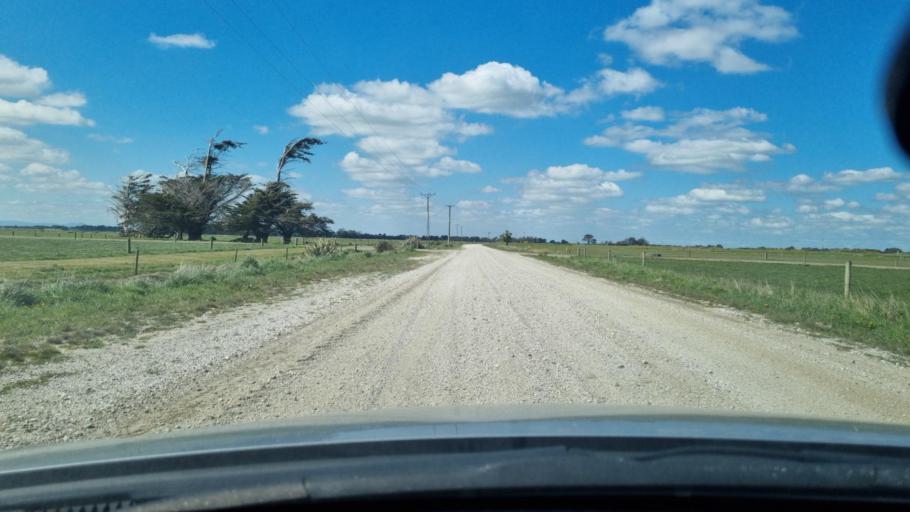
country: NZ
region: Southland
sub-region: Invercargill City
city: Invercargill
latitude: -46.3919
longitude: 168.2526
